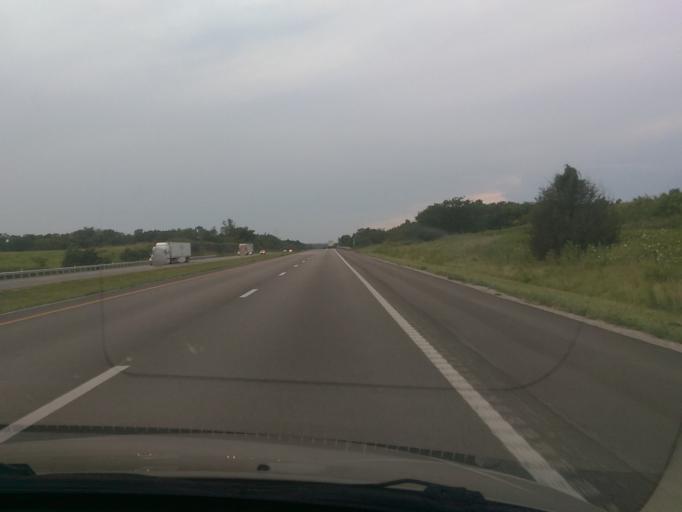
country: US
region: Missouri
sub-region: Andrew County
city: Savannah
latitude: 39.9504
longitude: -94.9494
